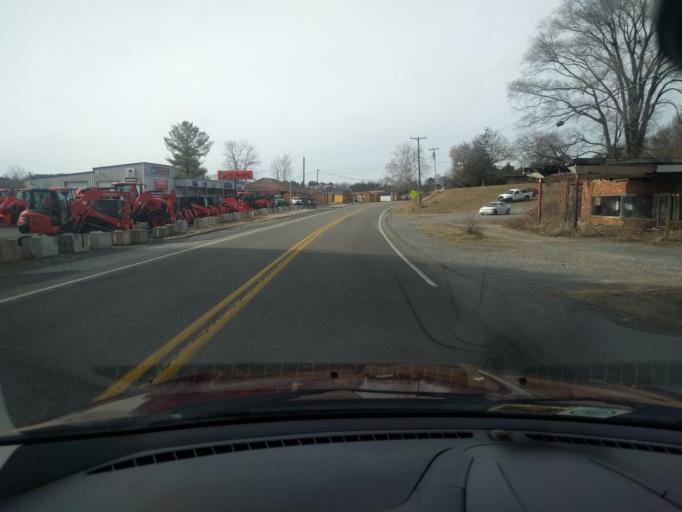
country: US
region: Virginia
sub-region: Augusta County
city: Stuarts Draft
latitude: 38.0309
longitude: -79.0596
